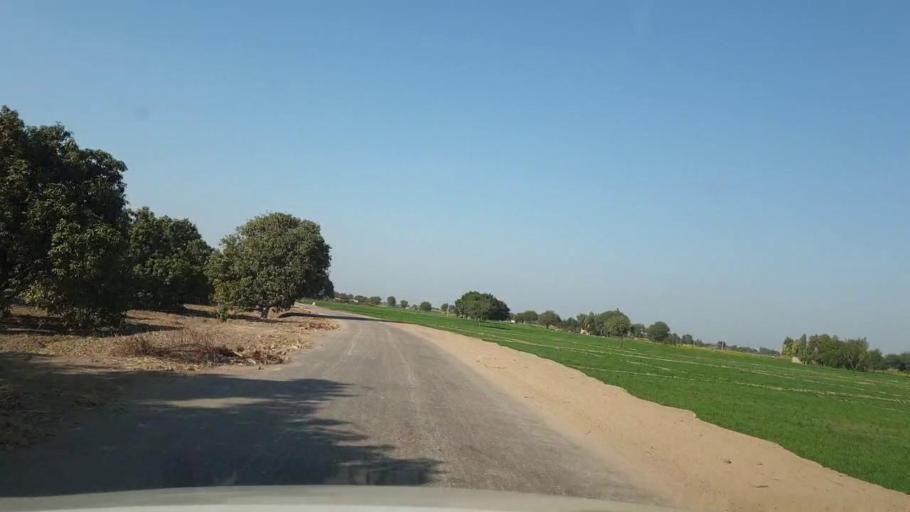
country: PK
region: Sindh
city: Tando Allahyar
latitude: 25.4915
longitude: 68.6547
